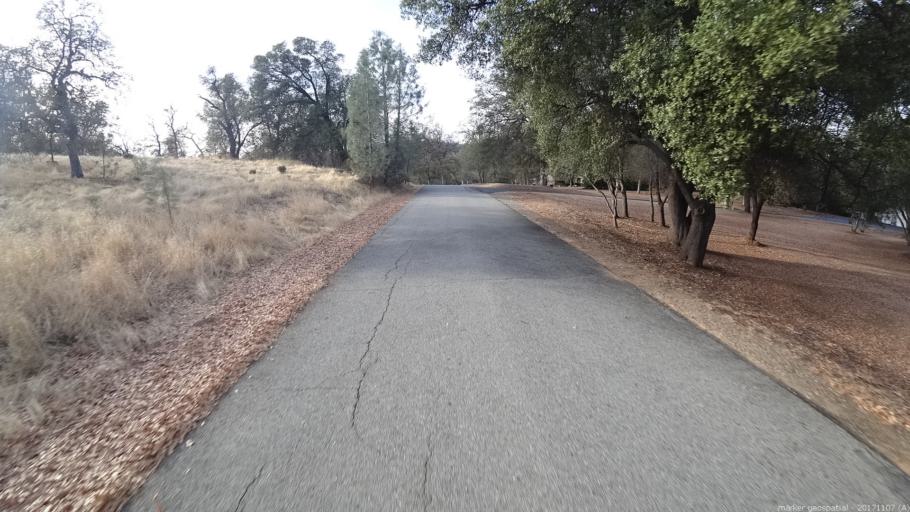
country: US
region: California
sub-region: Shasta County
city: Shasta
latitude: 40.5134
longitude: -122.4738
